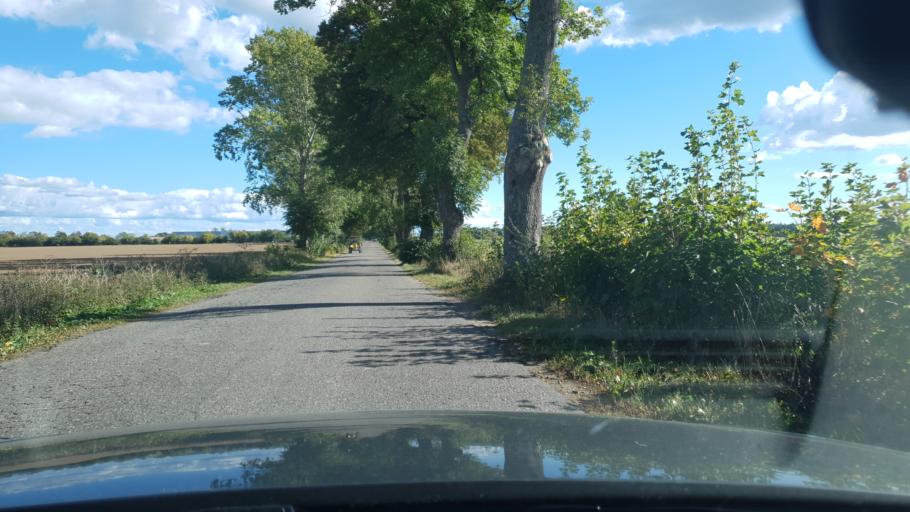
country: PL
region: Pomeranian Voivodeship
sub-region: Powiat pucki
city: Zelistrzewo
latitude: 54.6875
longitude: 18.4410
